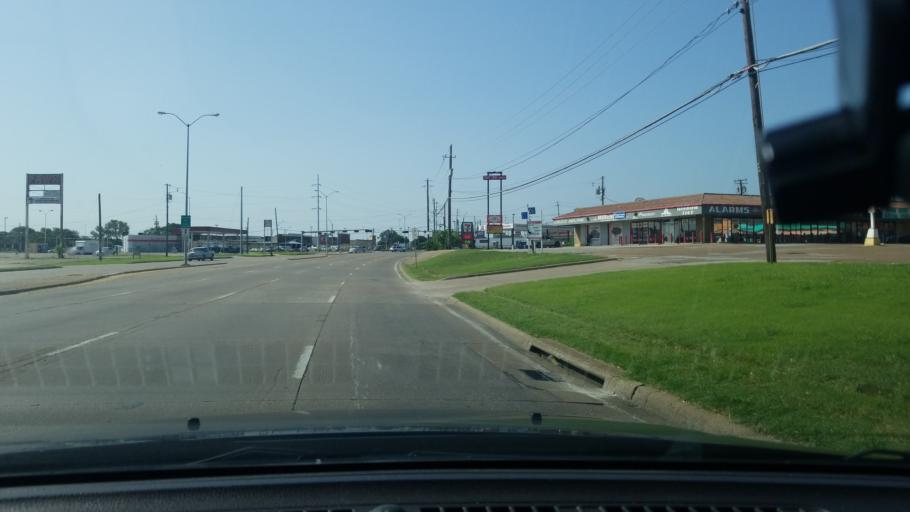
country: US
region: Texas
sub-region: Dallas County
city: Mesquite
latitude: 32.8086
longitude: -96.6836
